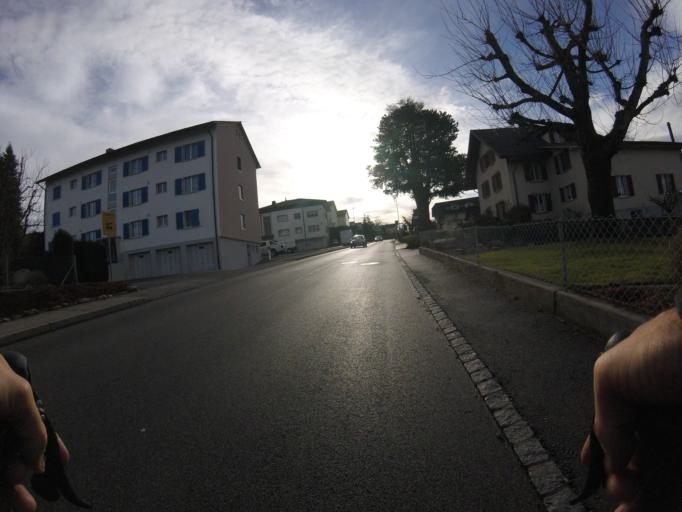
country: CH
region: Fribourg
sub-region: Sense District
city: Ueberstorf
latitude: 46.8629
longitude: 7.3129
